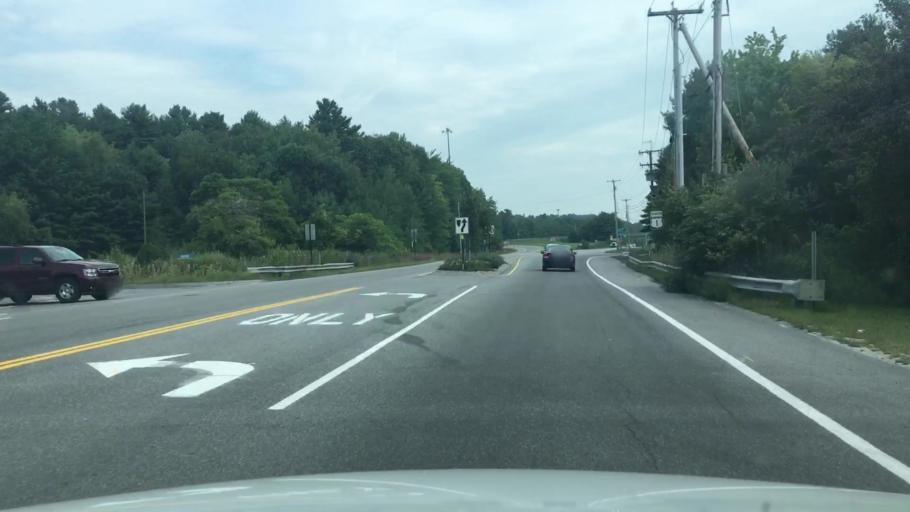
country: US
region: Maine
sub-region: Cumberland County
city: Falmouth
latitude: 43.7265
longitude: -70.2312
